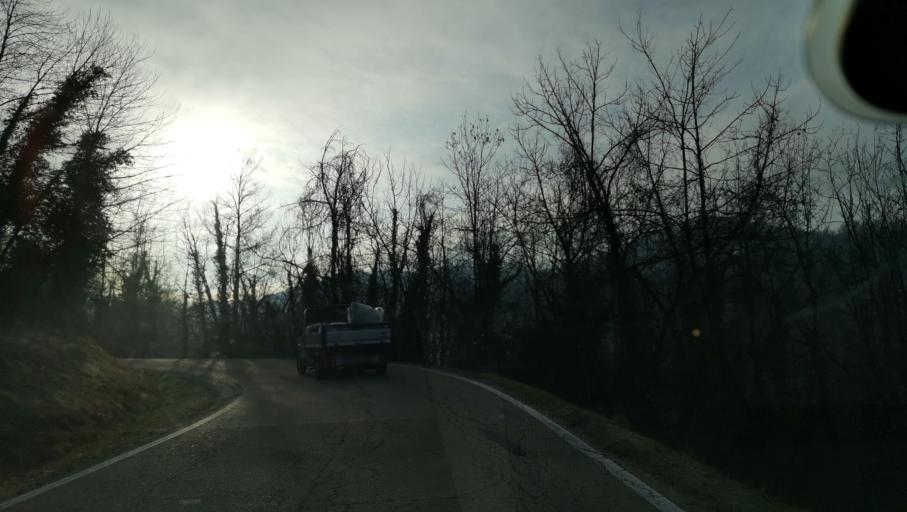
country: IT
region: Piedmont
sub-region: Provincia di Asti
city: Berzano di San Pietro
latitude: 45.1021
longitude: 7.9403
